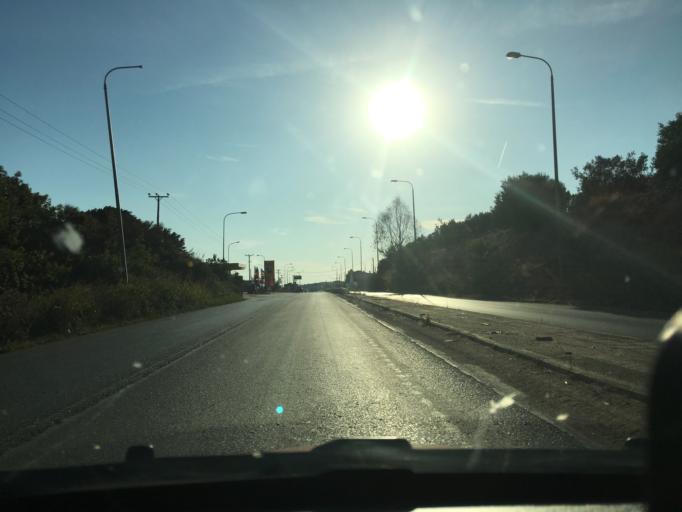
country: GR
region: Central Macedonia
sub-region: Nomos Chalkidikis
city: Nea Moudhania
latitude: 40.2461
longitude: 23.3058
